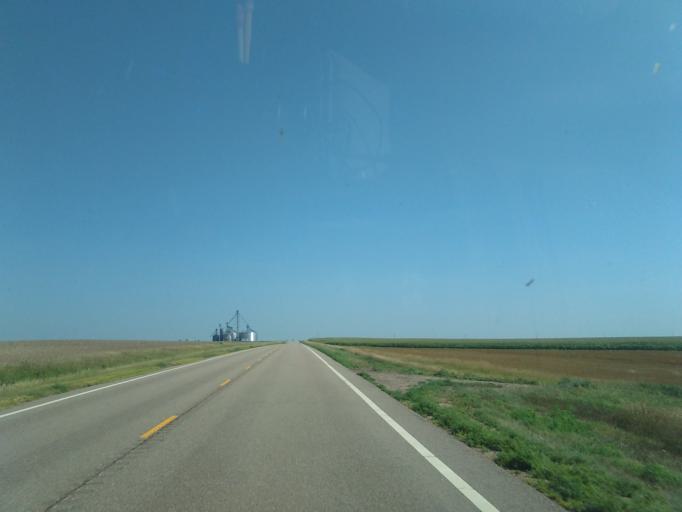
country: US
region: Kansas
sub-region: Cheyenne County
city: Saint Francis
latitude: 39.6195
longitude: -101.7128
